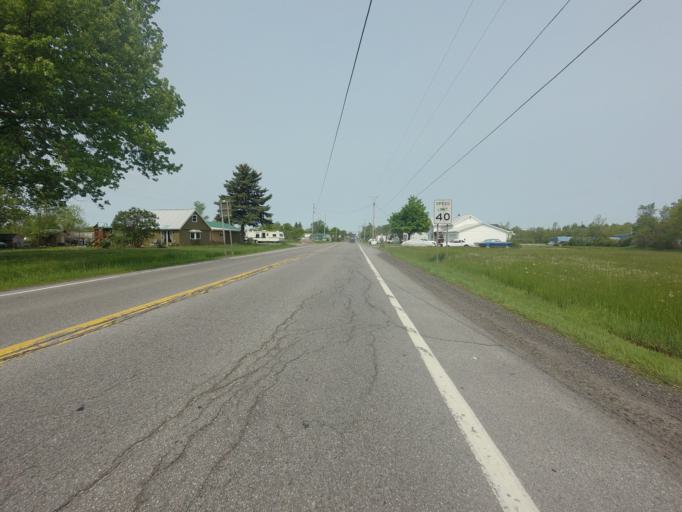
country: US
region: New York
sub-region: Jefferson County
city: Dexter
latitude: 44.0275
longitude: -76.0429
